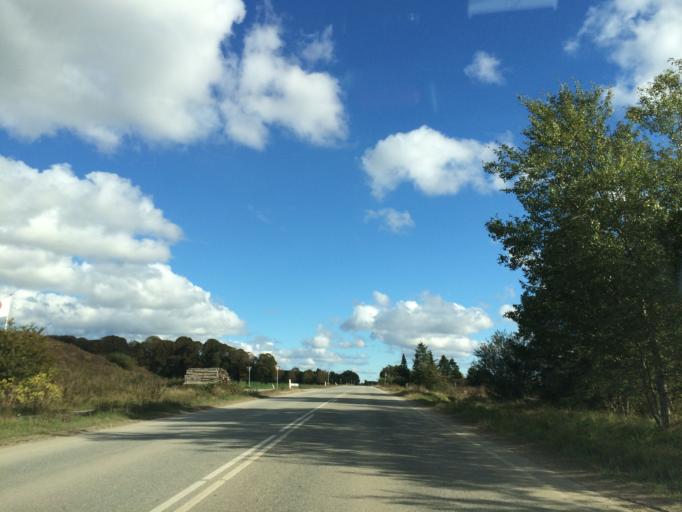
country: DK
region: Central Jutland
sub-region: Skanderborg Kommune
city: Ry
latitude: 56.1494
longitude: 9.7730
